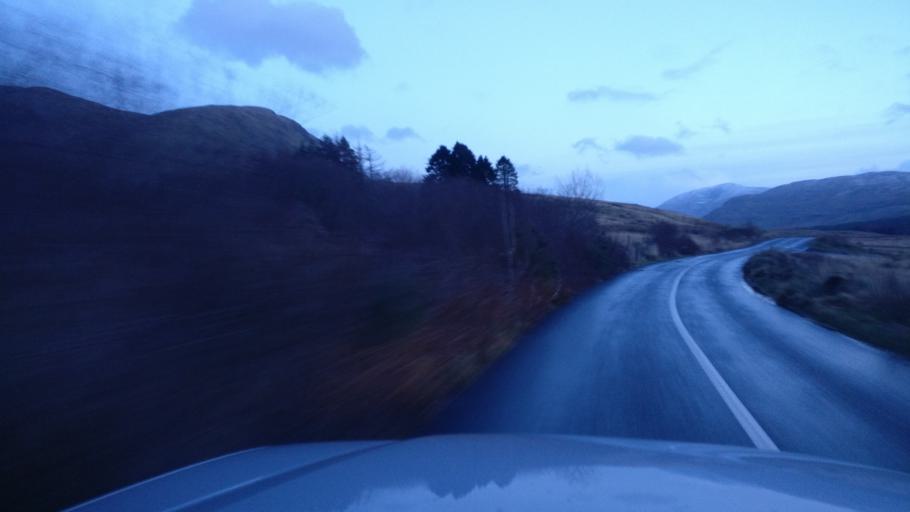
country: IE
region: Connaught
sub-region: Maigh Eo
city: Westport
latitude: 53.5529
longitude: -9.6358
